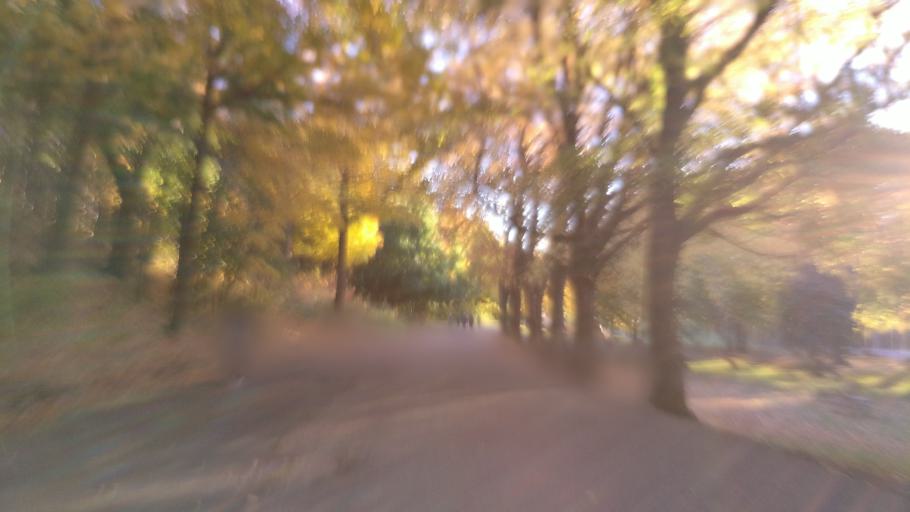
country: CA
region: Quebec
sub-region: Montreal
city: Montreal
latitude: 45.5019
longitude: -73.5923
